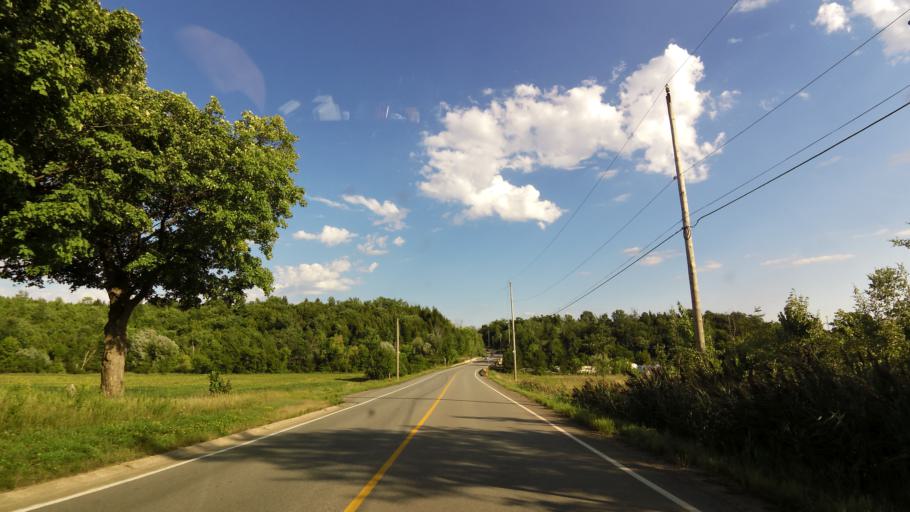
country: CA
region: Ontario
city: Brampton
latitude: 43.7390
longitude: -79.9275
